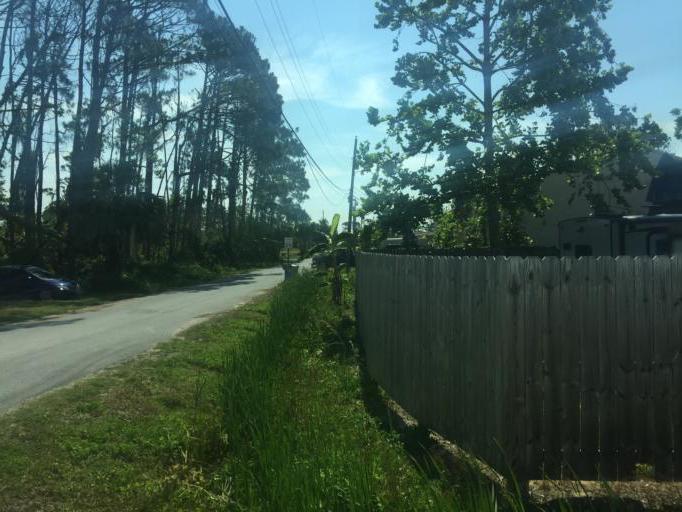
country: US
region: Florida
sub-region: Bay County
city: Lower Grand Lagoon
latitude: 30.1565
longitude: -85.7542
